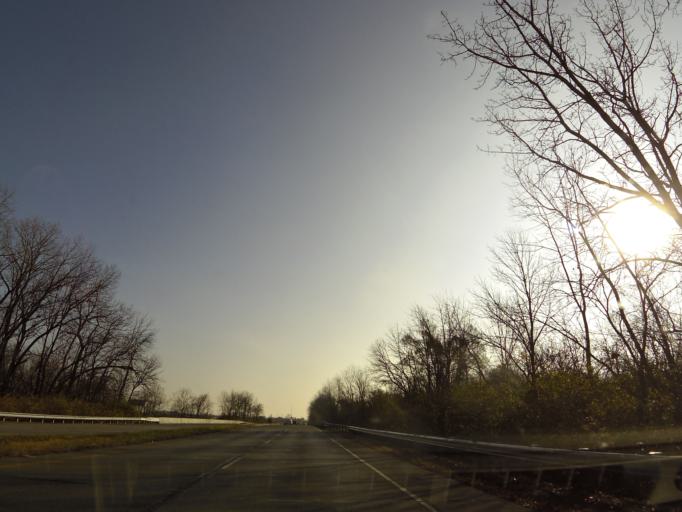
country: US
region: Indiana
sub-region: Marion County
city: Speedway
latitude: 39.8045
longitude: -86.2880
